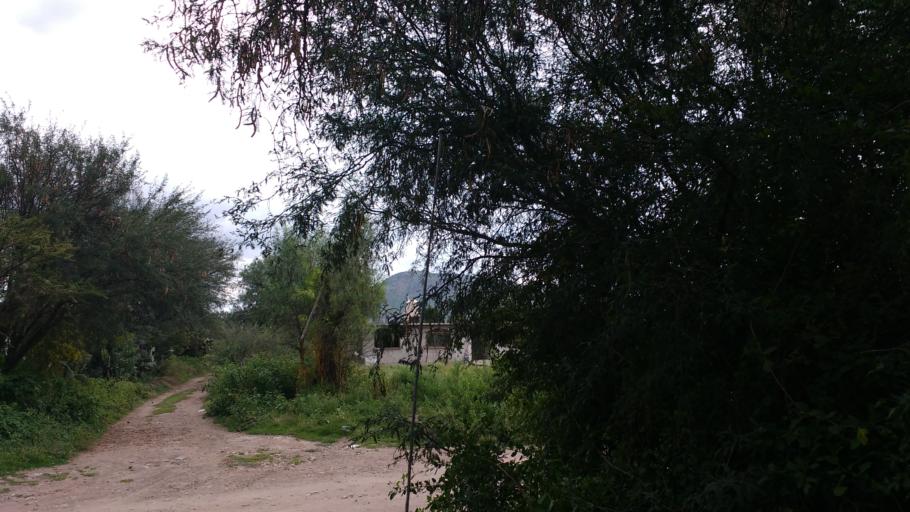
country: MX
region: Hidalgo
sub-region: Tezontepec de Aldama
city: Tenango
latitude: 20.2283
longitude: -99.2528
